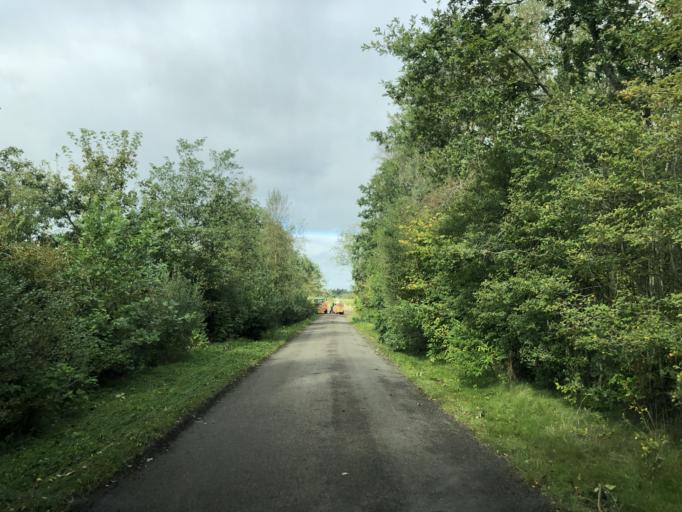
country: DK
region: Central Jutland
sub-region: Holstebro Kommune
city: Ulfborg
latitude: 56.2977
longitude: 8.4492
